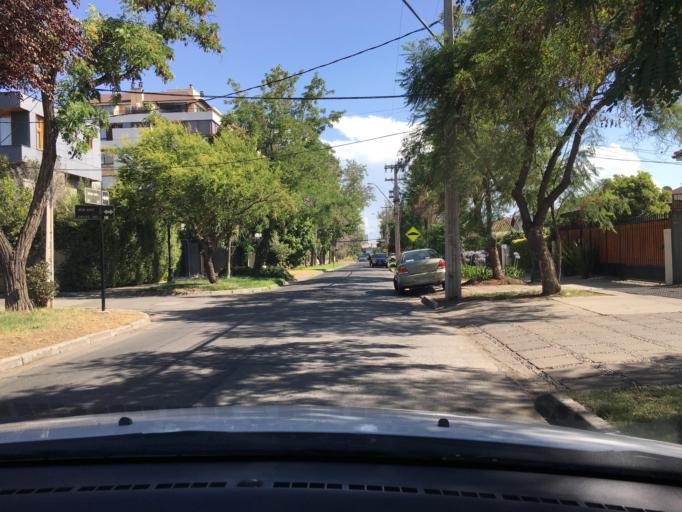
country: CL
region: Santiago Metropolitan
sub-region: Provincia de Santiago
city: Villa Presidente Frei, Nunoa, Santiago, Chile
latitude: -33.4418
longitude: -70.5908
